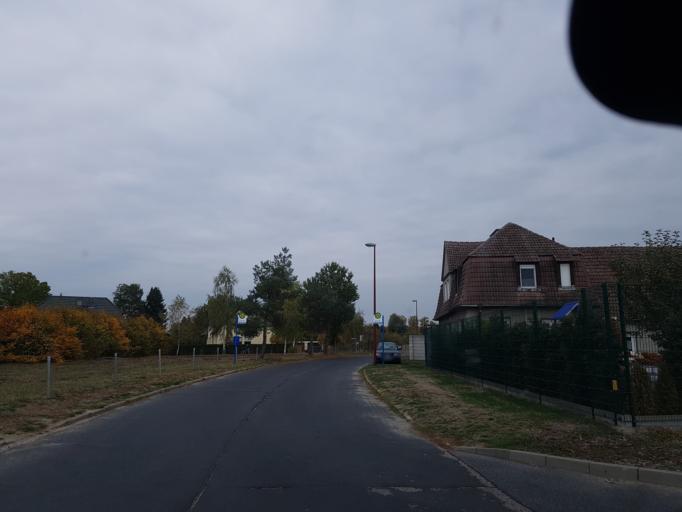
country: DE
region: Brandenburg
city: Finsterwalde
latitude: 51.6221
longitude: 13.6959
